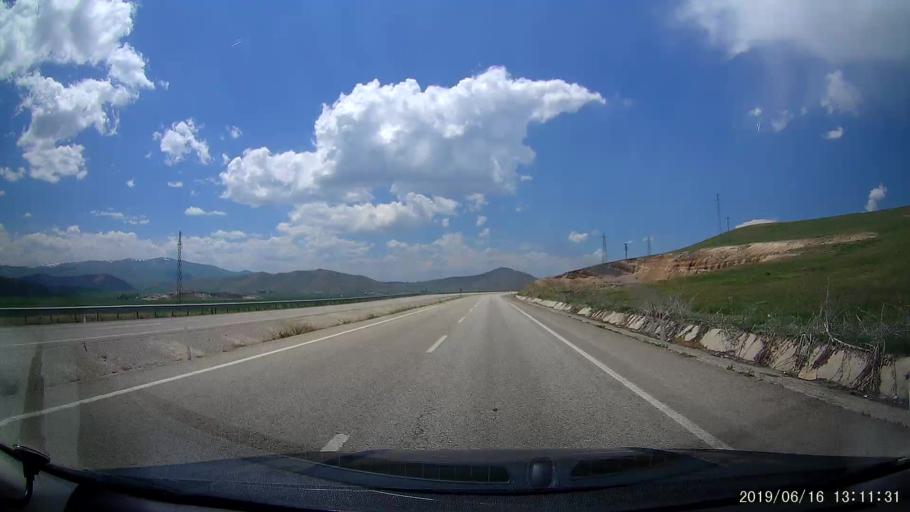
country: TR
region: Agri
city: Diyadin
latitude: 39.5919
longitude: 43.6053
